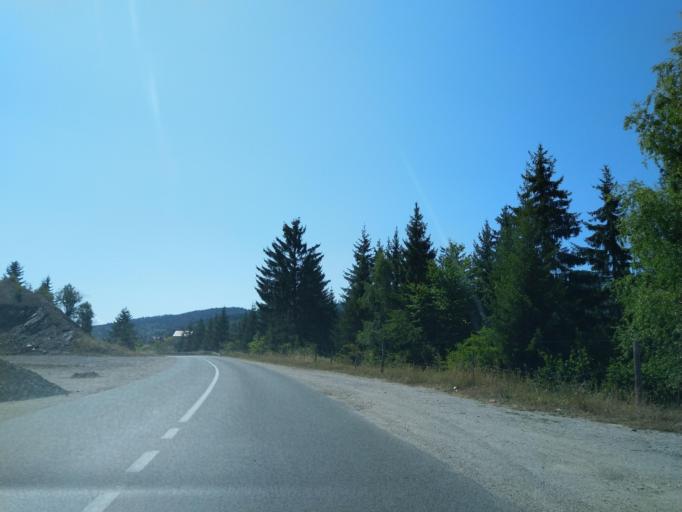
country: RS
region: Central Serbia
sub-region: Zlatiborski Okrug
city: Nova Varos
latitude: 43.4296
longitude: 19.8281
